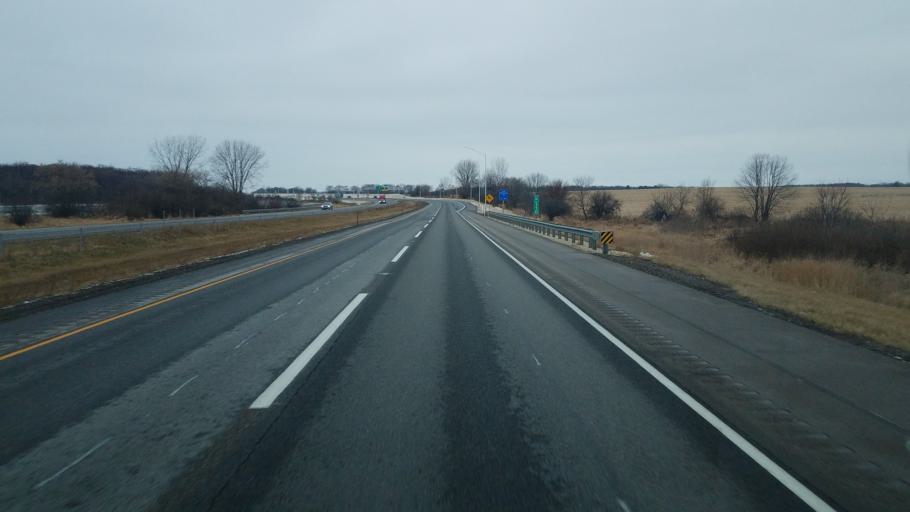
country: US
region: Illinois
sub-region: Kane County
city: Sugar Grove
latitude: 41.8150
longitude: -88.4530
